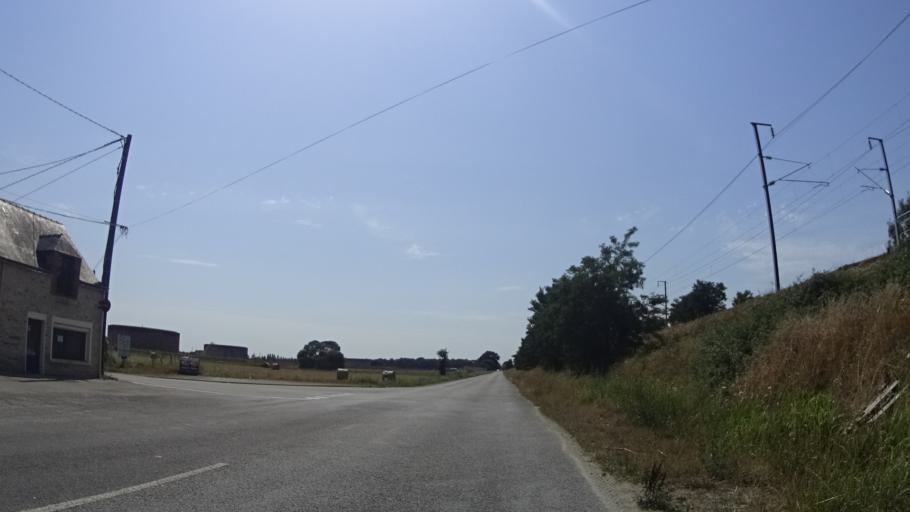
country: FR
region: Pays de la Loire
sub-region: Departement de la Loire-Atlantique
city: La Chapelle-Launay
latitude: 47.3580
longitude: -1.9756
